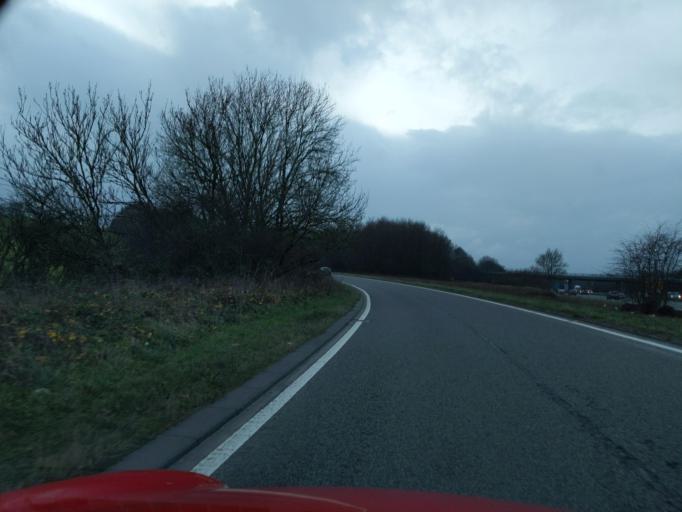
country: GB
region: England
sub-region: Devon
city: Yealmpton
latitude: 50.3793
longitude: -4.0204
